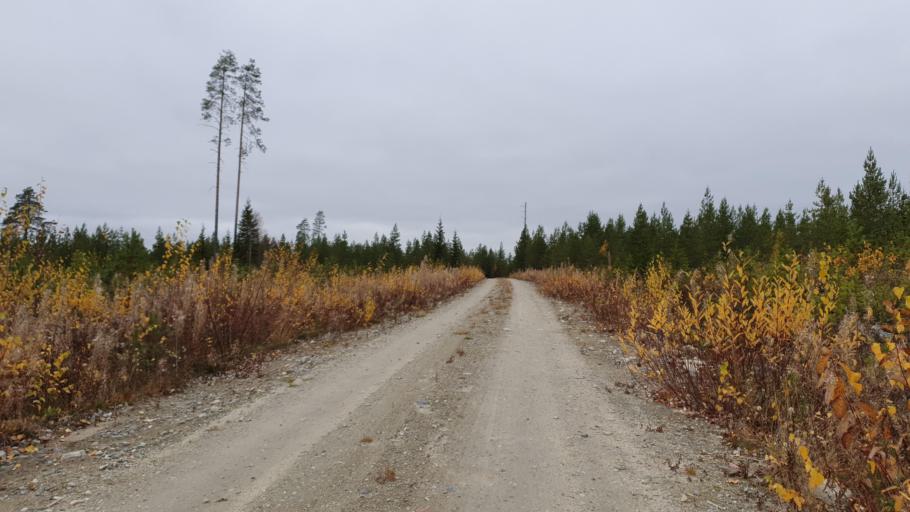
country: FI
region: Kainuu
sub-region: Kehys-Kainuu
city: Kuhmo
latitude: 64.4473
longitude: 29.6193
